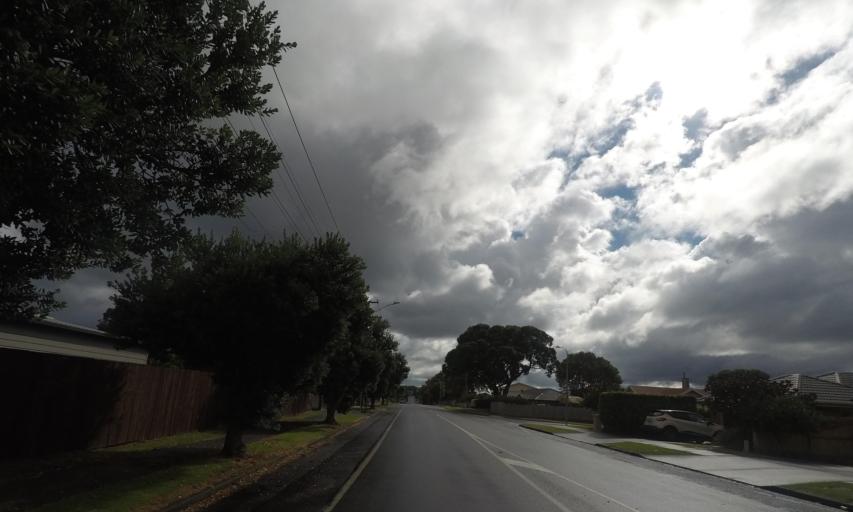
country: NZ
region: Auckland
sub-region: Auckland
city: Mangere
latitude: -36.9580
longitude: 174.7838
